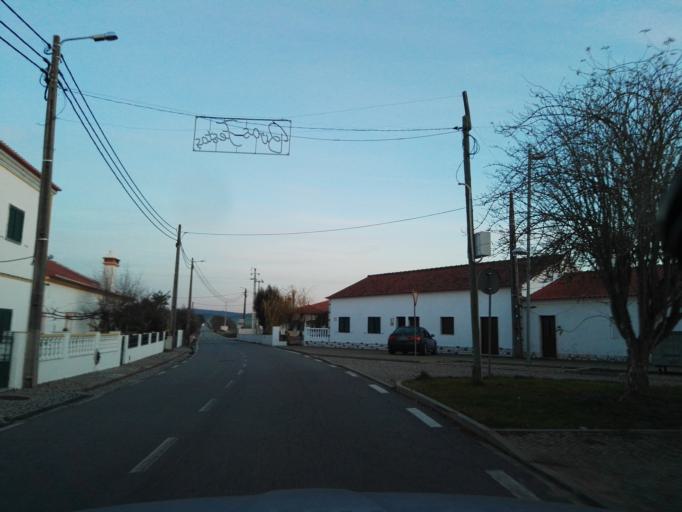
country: PT
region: Evora
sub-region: Arraiolos
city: Arraiolos
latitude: 38.7636
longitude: -8.1200
